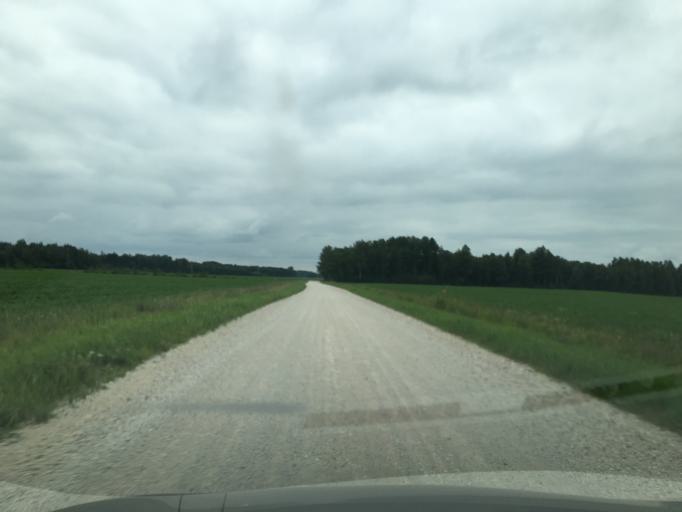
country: EE
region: Raplamaa
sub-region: Jaervakandi vald
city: Jarvakandi
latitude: 58.7959
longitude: 24.9599
